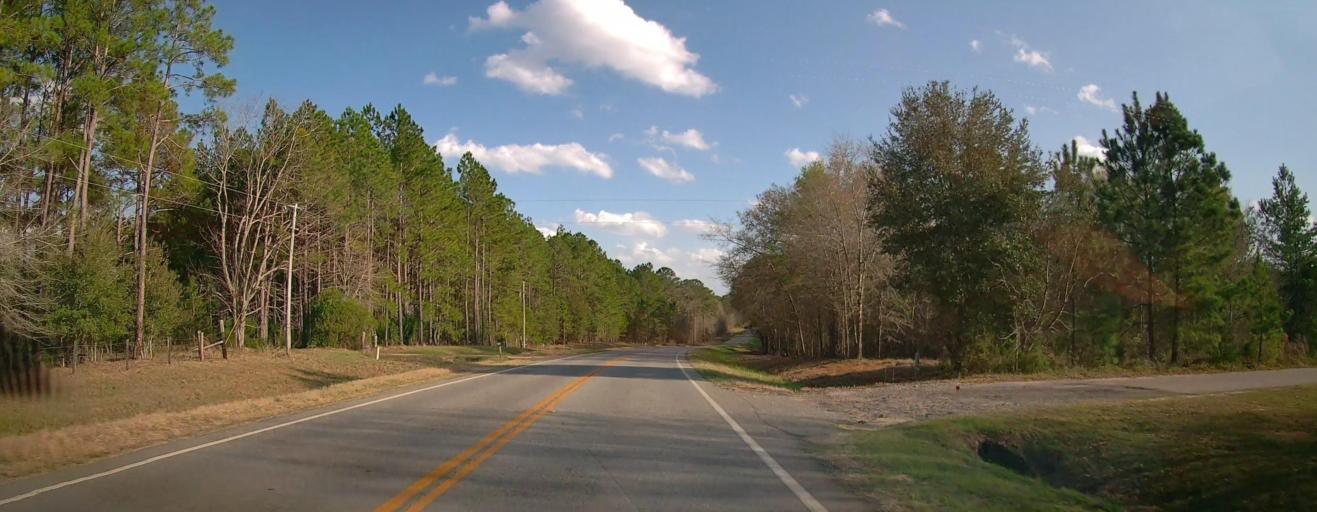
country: US
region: Georgia
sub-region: Toombs County
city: Lyons
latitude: 32.1717
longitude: -82.2755
